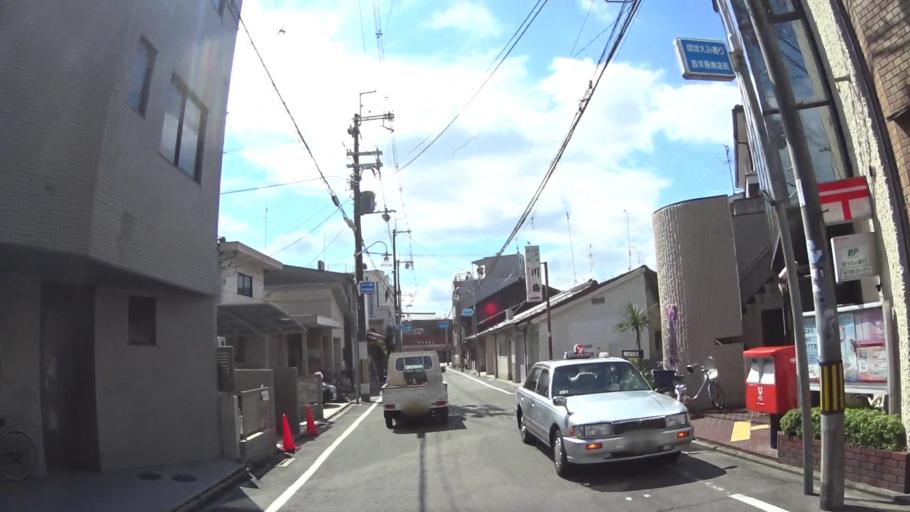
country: JP
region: Kyoto
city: Muko
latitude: 34.9901
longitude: 135.7184
